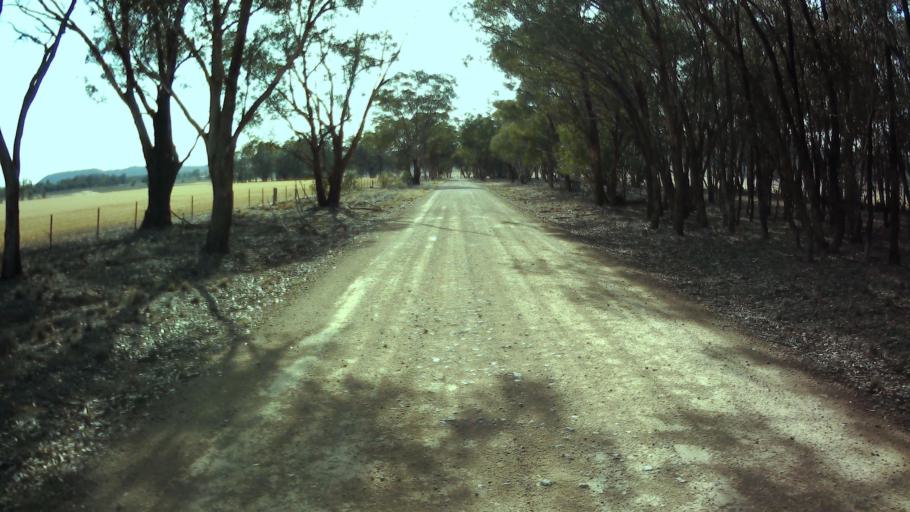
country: AU
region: New South Wales
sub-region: Weddin
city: Grenfell
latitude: -33.7974
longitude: 148.0898
